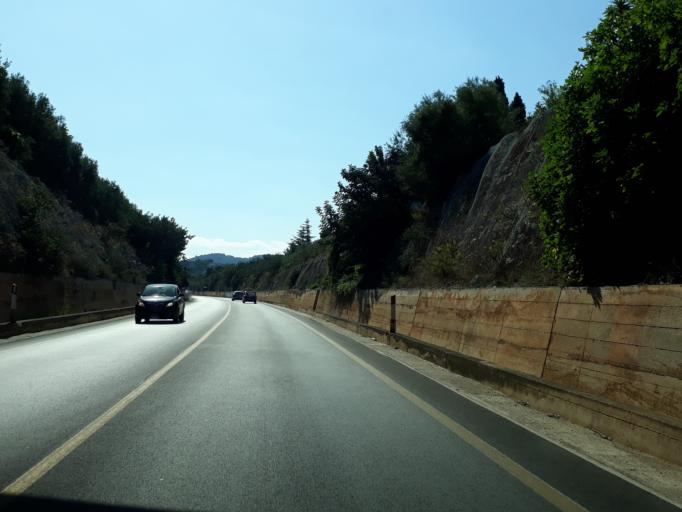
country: IT
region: Apulia
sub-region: Provincia di Brindisi
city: Fasano
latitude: 40.8372
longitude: 17.3507
